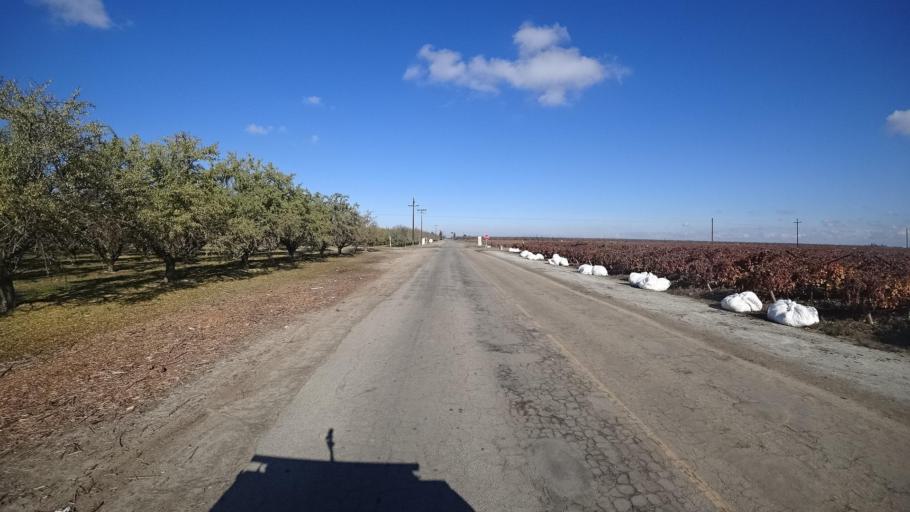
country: US
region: California
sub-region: Kern County
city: McFarland
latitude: 35.6882
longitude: -119.2587
